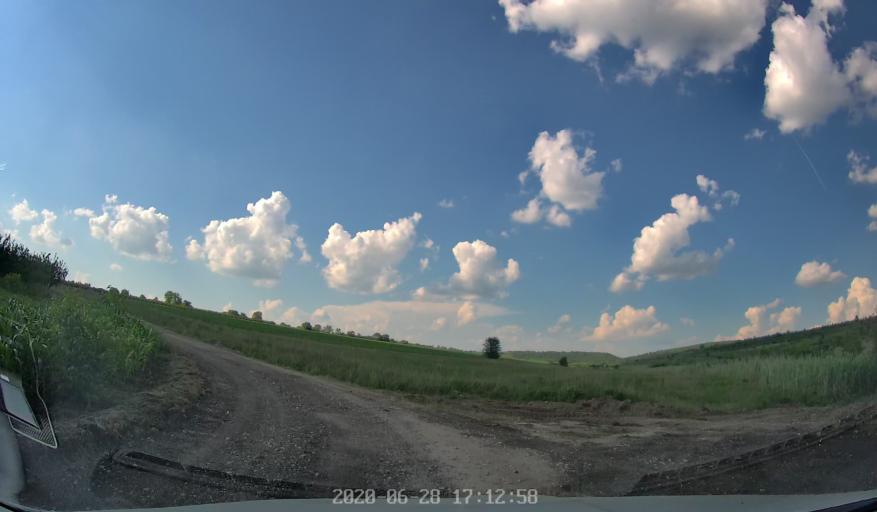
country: MD
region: Chisinau
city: Vatra
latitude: 46.9899
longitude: 28.6985
